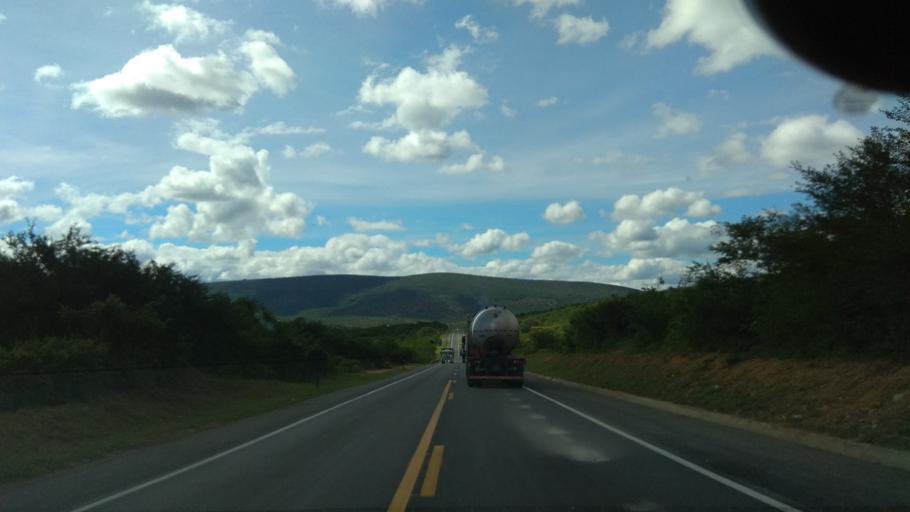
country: BR
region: Bahia
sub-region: Santa Ines
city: Santa Ines
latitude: -13.2836
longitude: -40.0191
